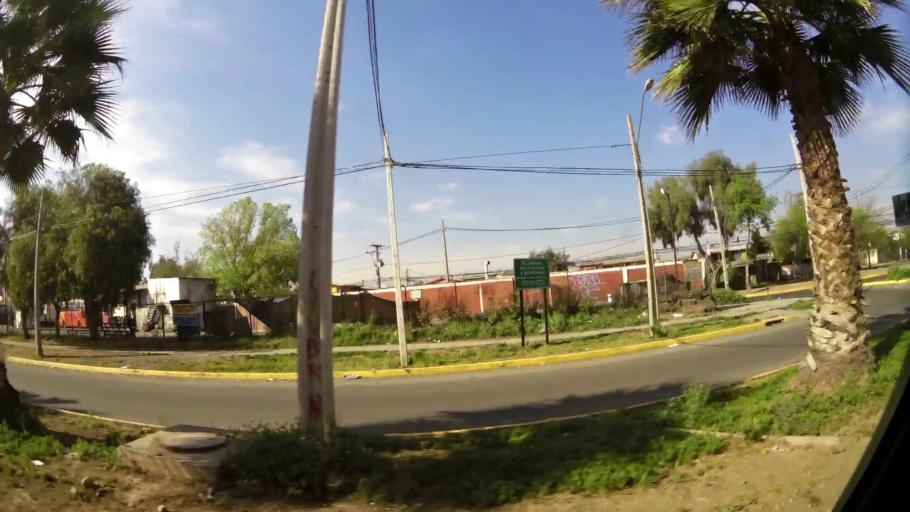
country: CL
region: Santiago Metropolitan
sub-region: Provincia de Santiago
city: Lo Prado
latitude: -33.4540
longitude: -70.7592
